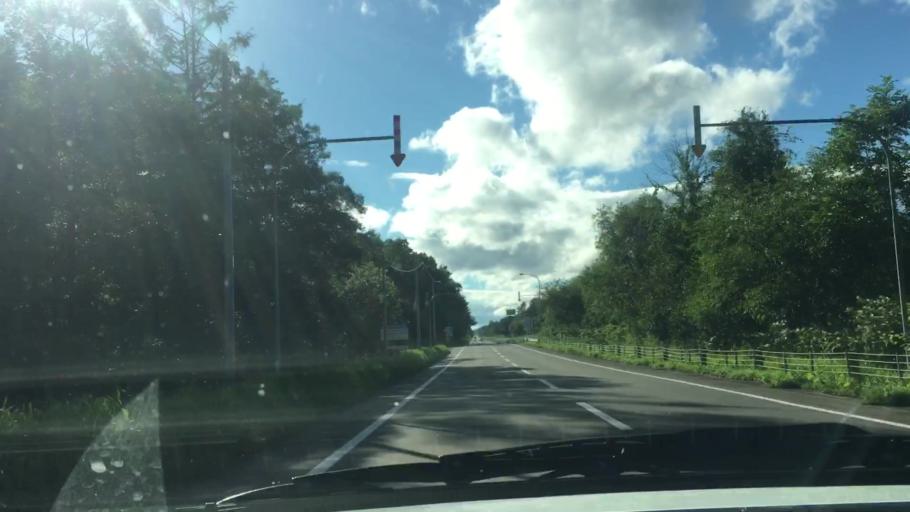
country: JP
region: Hokkaido
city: Otofuke
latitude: 43.1663
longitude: 143.1323
